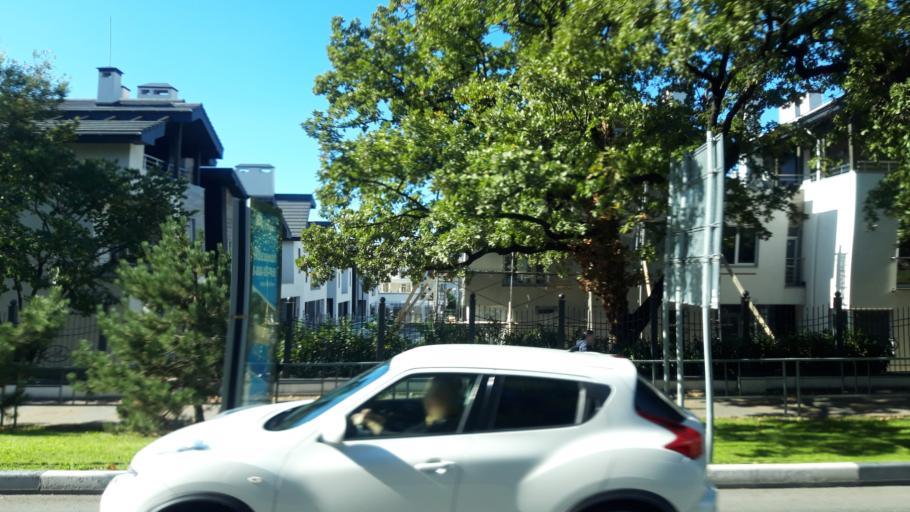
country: RU
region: Krasnodarskiy
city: Gelendzhik
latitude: 44.5689
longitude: 38.0787
